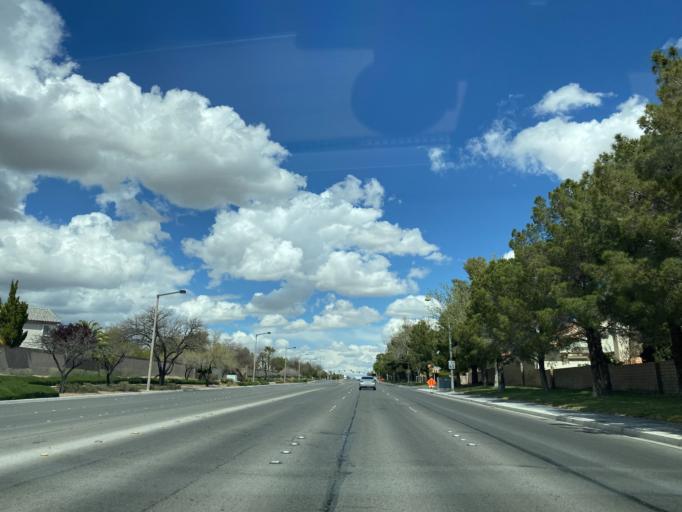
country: US
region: Nevada
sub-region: Clark County
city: Summerlin South
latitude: 36.1408
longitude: -115.3153
